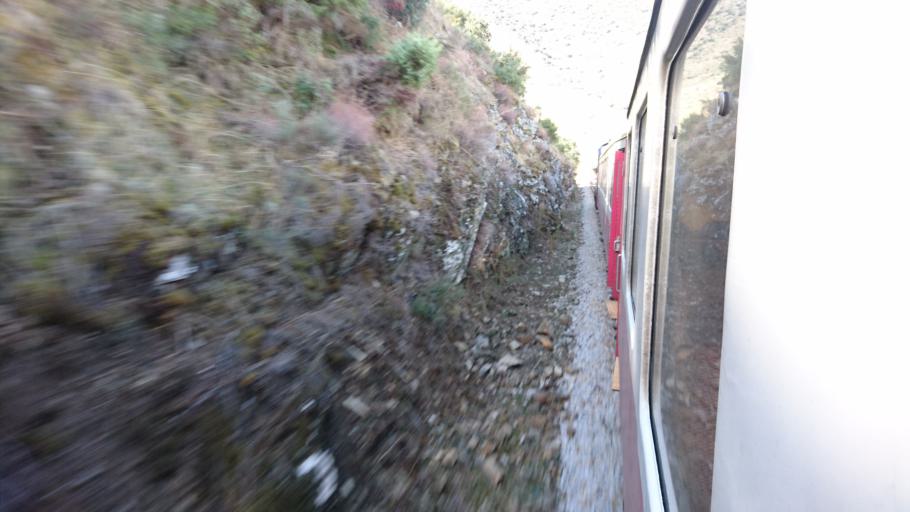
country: PT
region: Guarda
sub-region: Vila Nova de Foz Coa
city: Vila Nova de Foz Coa
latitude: 41.1250
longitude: -7.1934
